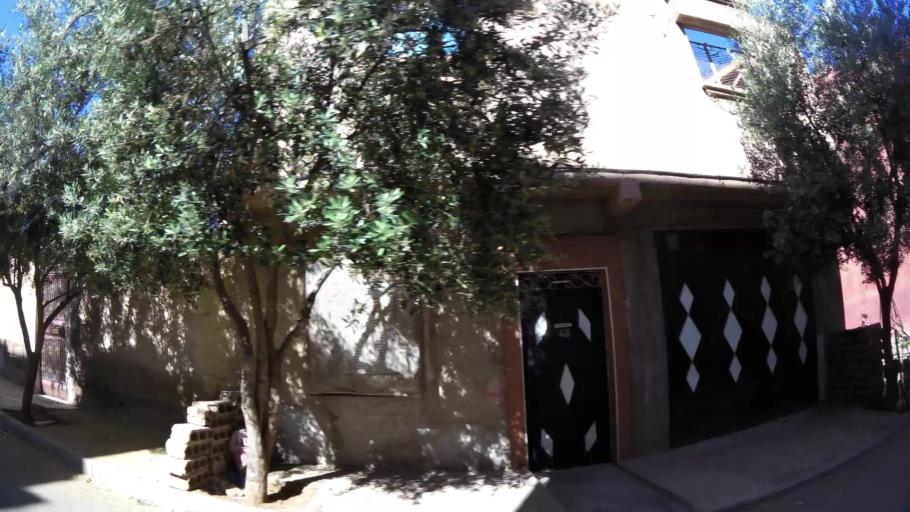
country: MA
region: Oriental
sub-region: Oujda-Angad
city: Oujda
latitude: 34.6548
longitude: -1.9497
